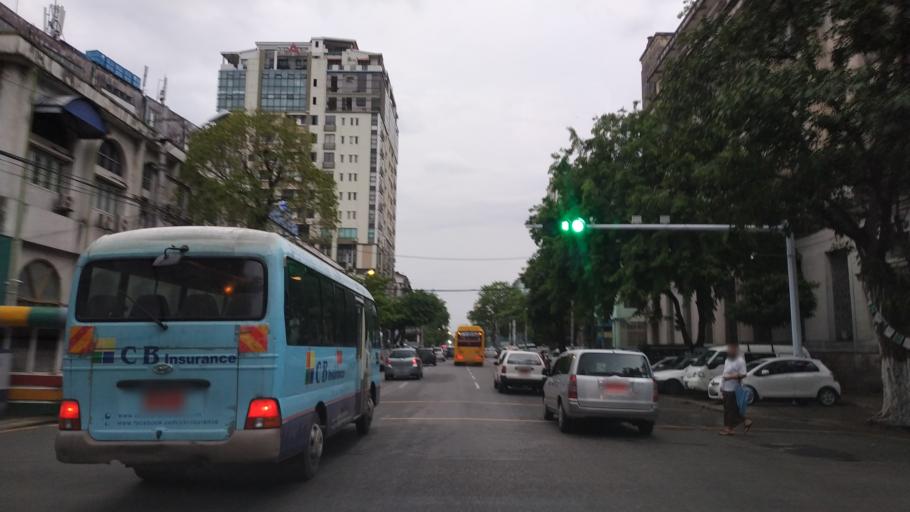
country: MM
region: Yangon
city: Yangon
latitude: 16.7719
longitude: 96.1559
